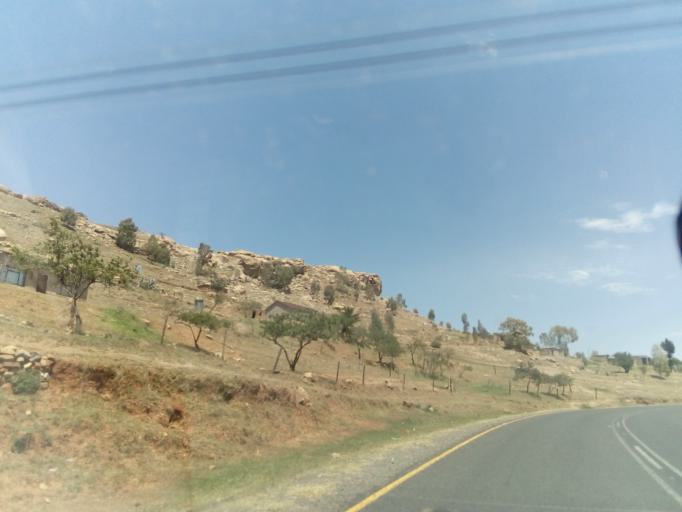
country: LS
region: Berea
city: Teyateyaneng
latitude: -29.1178
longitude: 27.8104
